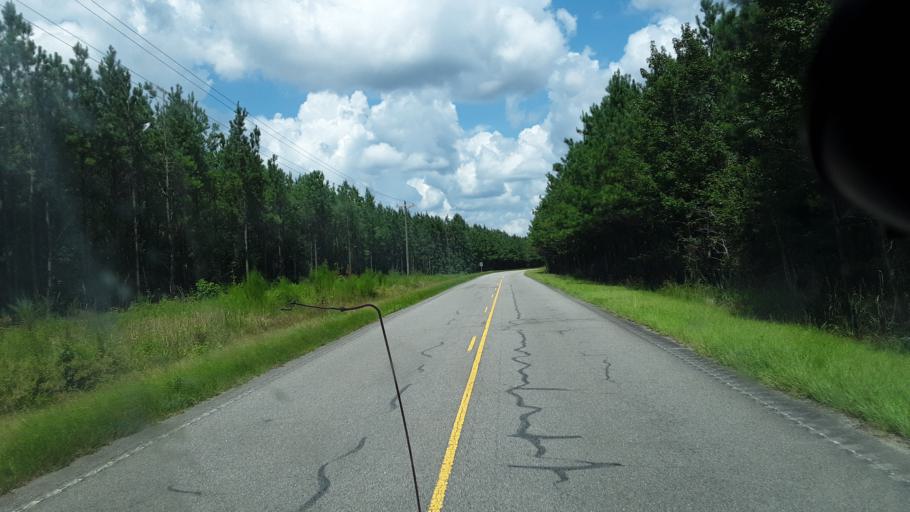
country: US
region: South Carolina
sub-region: Williamsburg County
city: Andrews
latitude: 33.5338
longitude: -79.4854
